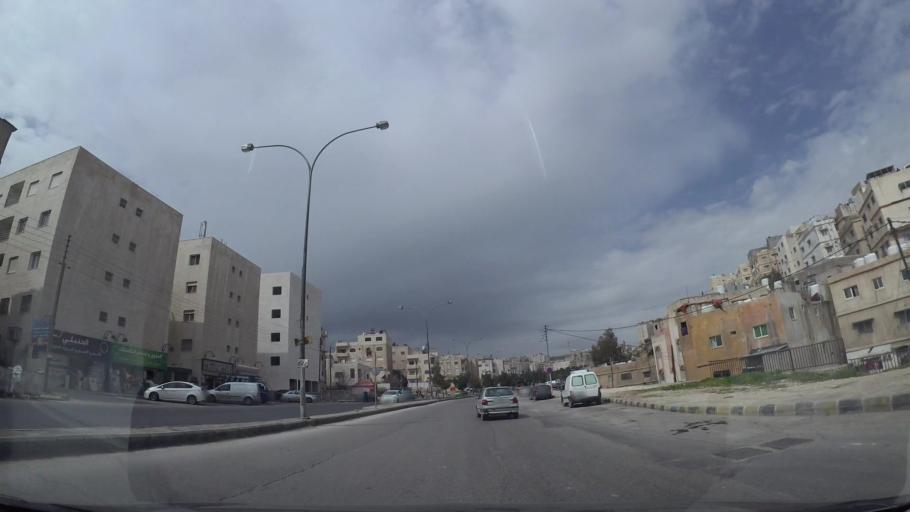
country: JO
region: Amman
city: Amman
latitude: 31.9752
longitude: 35.9204
